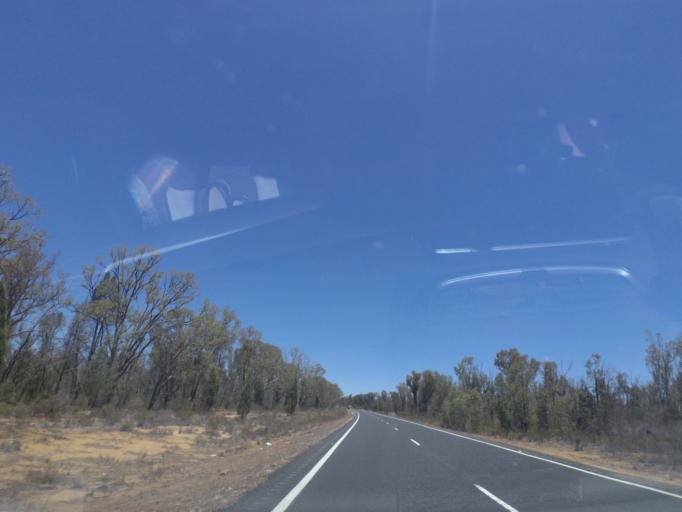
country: AU
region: New South Wales
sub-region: Warrumbungle Shire
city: Coonabarabran
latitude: -30.9428
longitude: 149.4232
